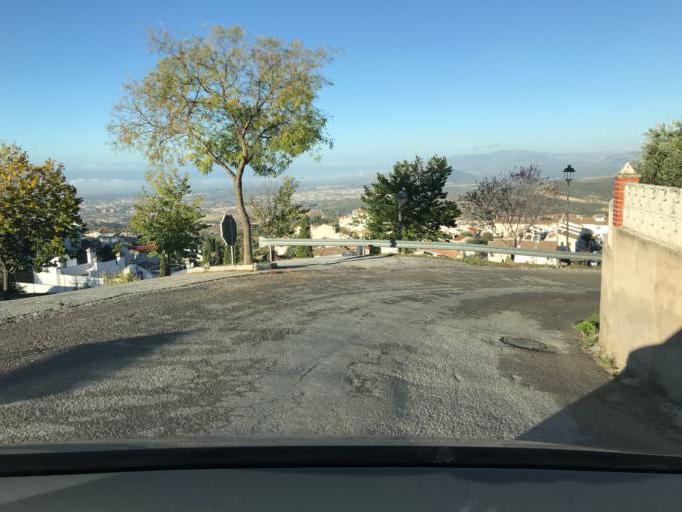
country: ES
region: Andalusia
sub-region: Provincia de Granada
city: Viznar
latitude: 37.2332
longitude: -3.5515
